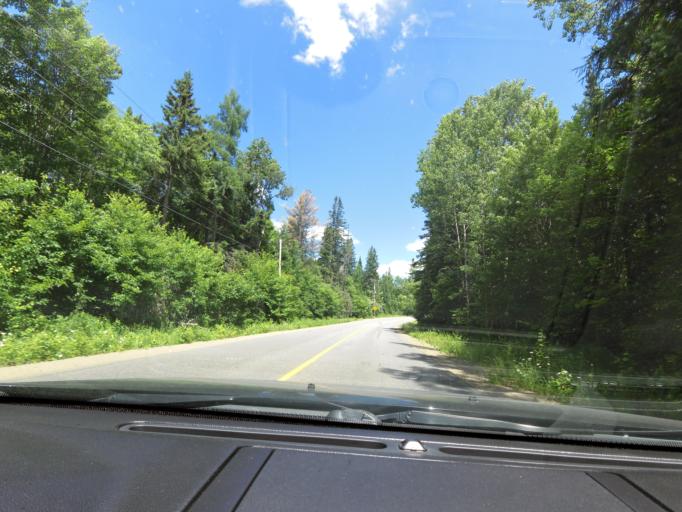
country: CA
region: Ontario
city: Huntsville
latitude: 45.5940
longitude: -79.2076
